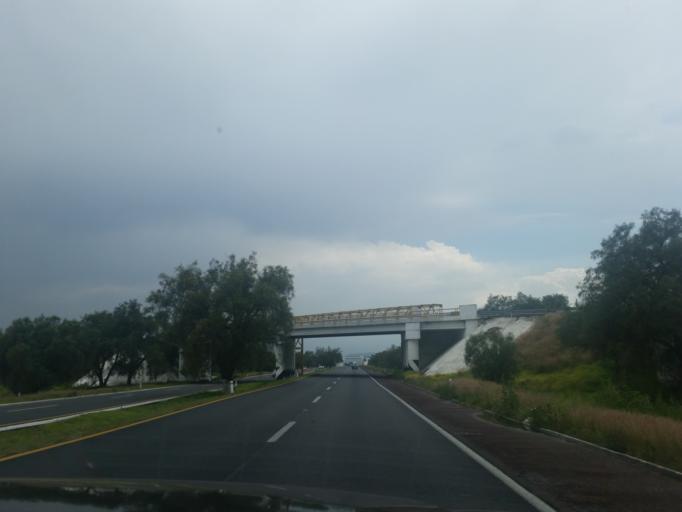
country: MX
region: Mexico
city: Acolman
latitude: 19.6257
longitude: -98.9328
